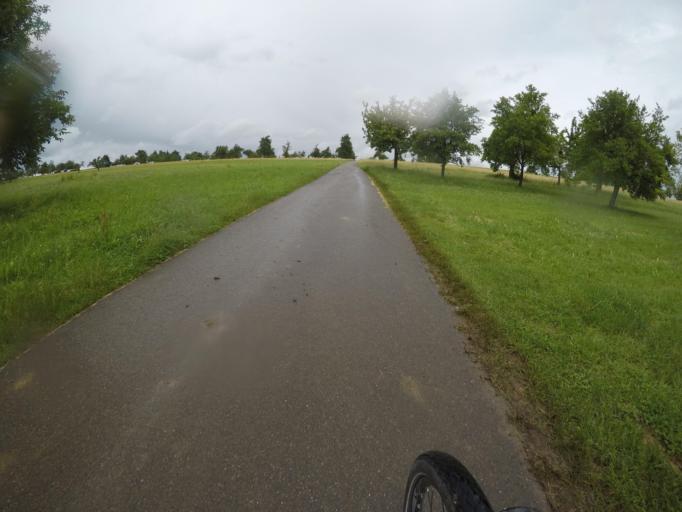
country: DE
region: Baden-Wuerttemberg
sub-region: Regierungsbezirk Stuttgart
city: Bondorf
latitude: 48.5565
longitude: 8.8284
